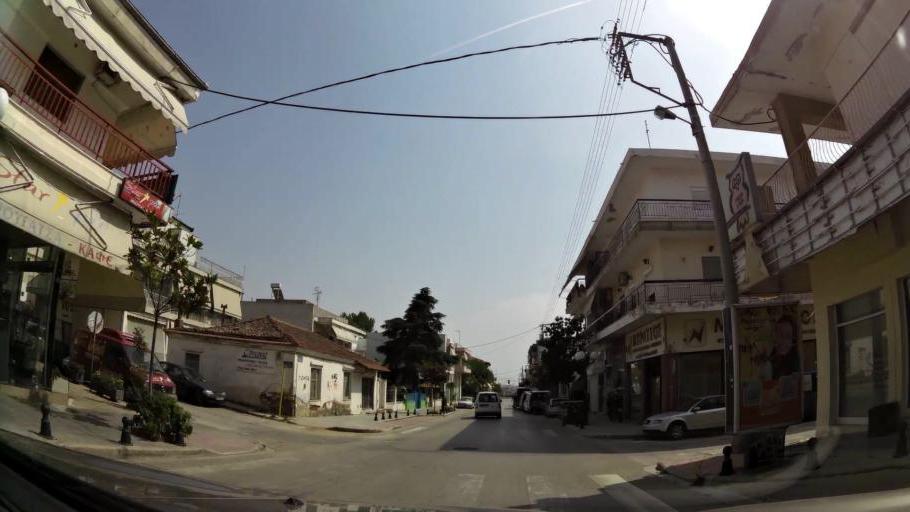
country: GR
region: Central Macedonia
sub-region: Nomos Thessalonikis
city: Efkarpia
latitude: 40.6895
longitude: 22.9549
